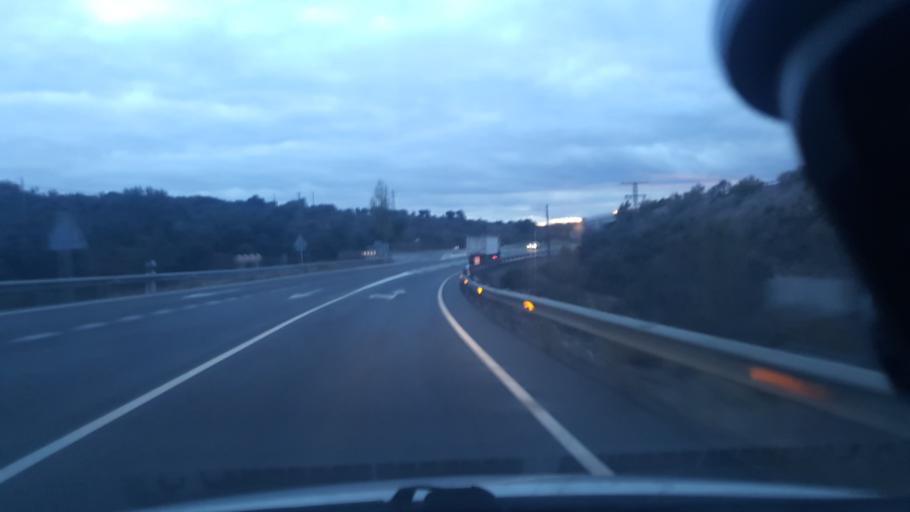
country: ES
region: Castille and Leon
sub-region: Provincia de Avila
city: Ojos-Albos
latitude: 40.7197
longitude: -4.5321
